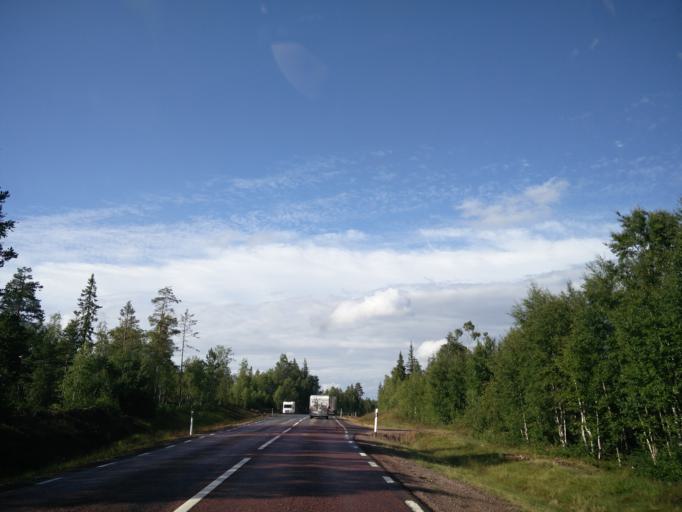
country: SE
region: Vaermland
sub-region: Hagfors Kommun
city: Ekshaerad
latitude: 60.4942
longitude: 13.4142
